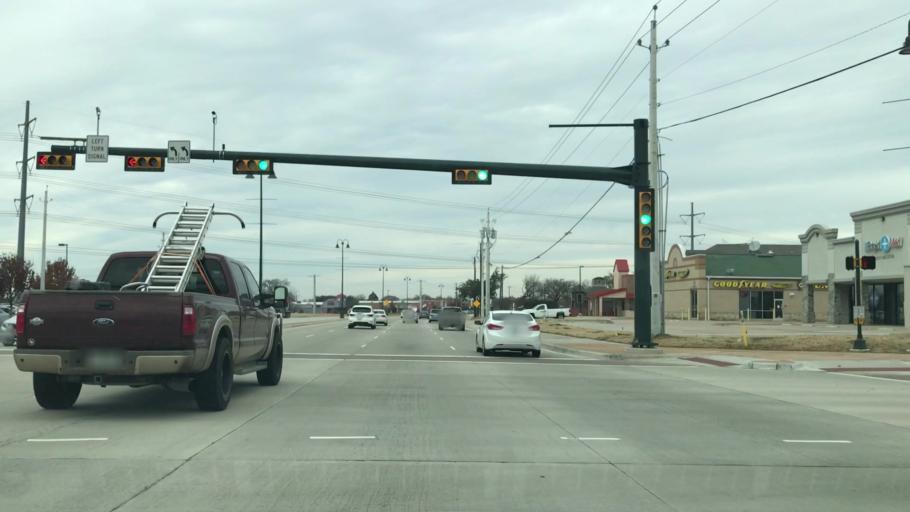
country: US
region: Texas
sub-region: Denton County
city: The Colony
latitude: 33.0690
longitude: -96.8908
